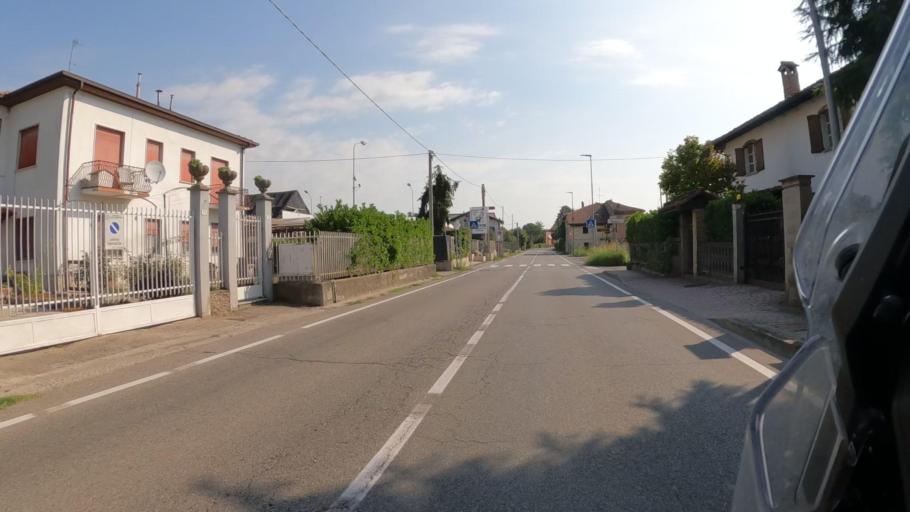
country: IT
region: Piedmont
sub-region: Provincia di Asti
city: Nizza Monferrato
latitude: 44.7777
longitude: 8.3645
